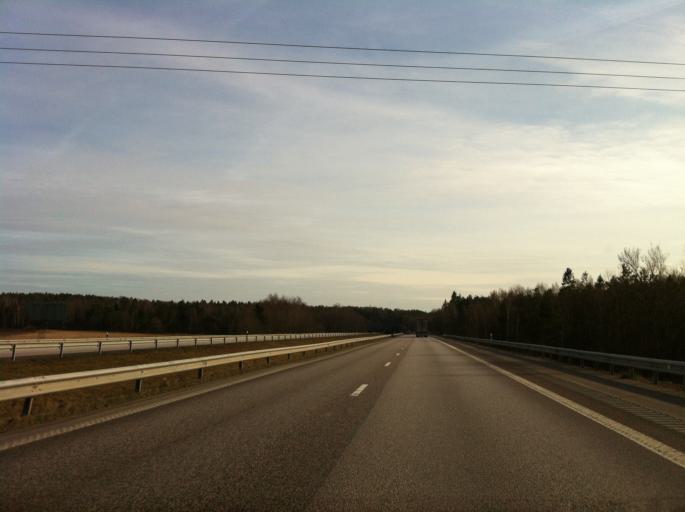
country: SE
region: Halland
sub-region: Kungsbacka Kommun
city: Fjaeras kyrkby
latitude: 57.4328
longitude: 12.1518
